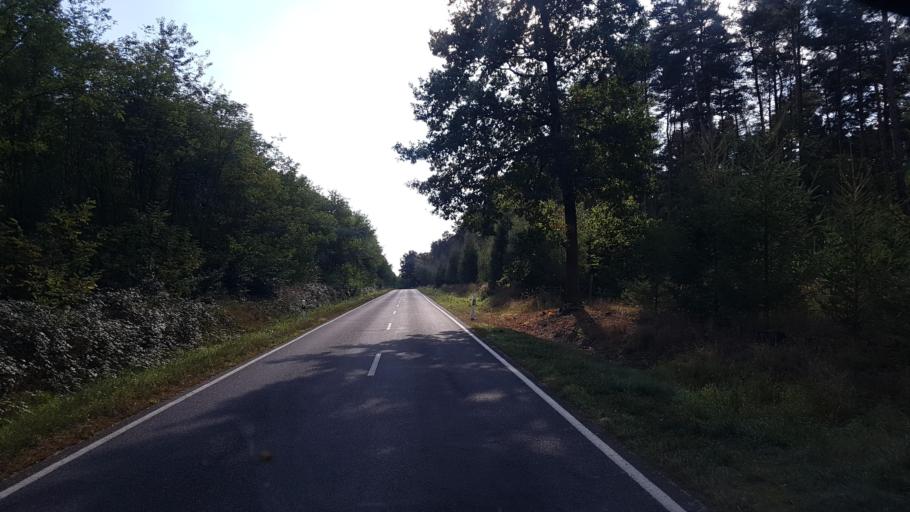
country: DE
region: Brandenburg
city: Vetschau
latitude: 51.7275
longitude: 14.0986
